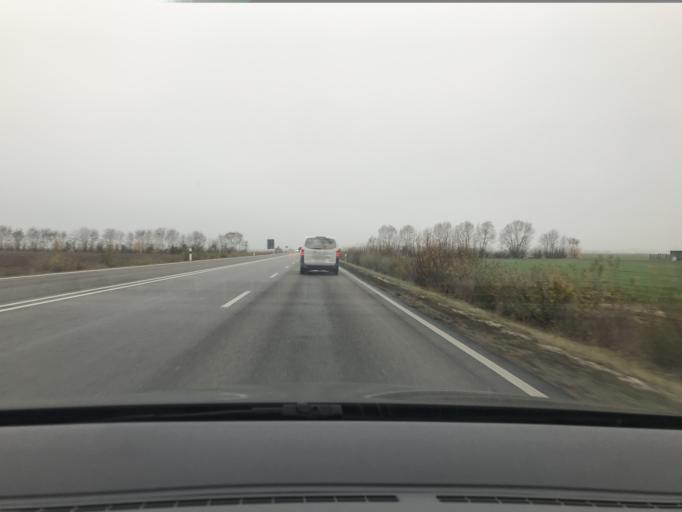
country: DE
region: Bavaria
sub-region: Swabia
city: Wallerstein
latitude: 48.8699
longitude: 10.4705
